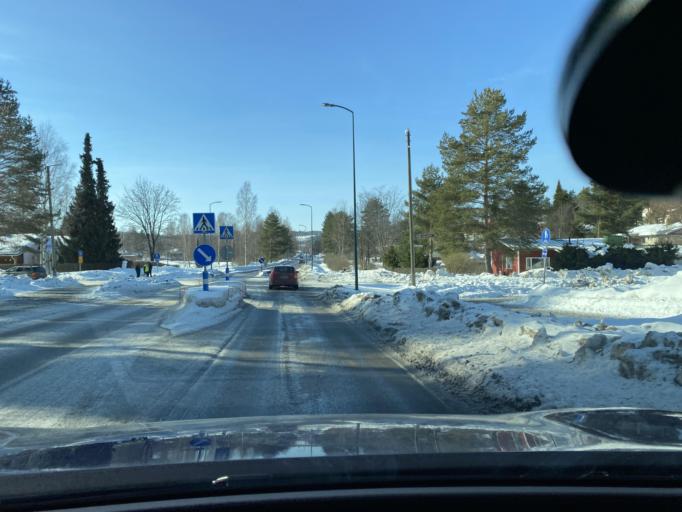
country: FI
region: Central Finland
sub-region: Jyvaeskylae
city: Korpilahti
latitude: 62.0180
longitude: 25.5693
